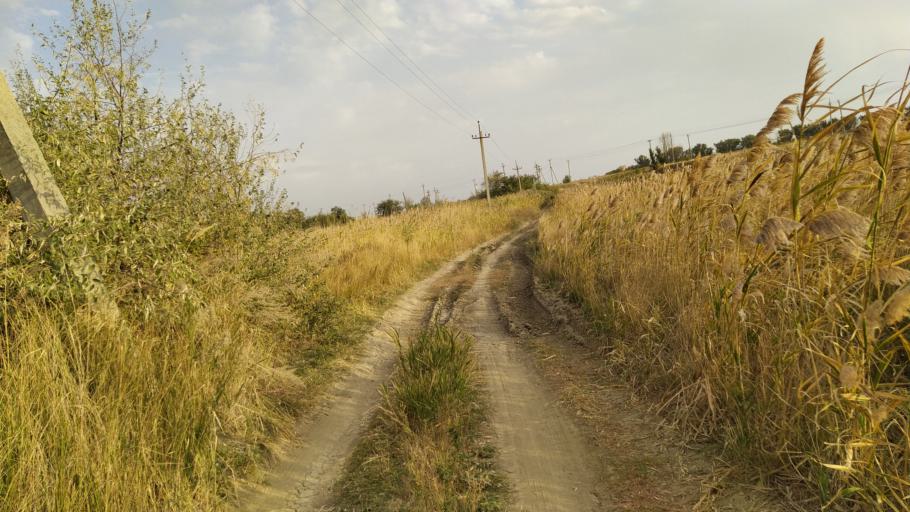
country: RU
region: Rostov
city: Kuleshovka
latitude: 47.1104
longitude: 39.6121
